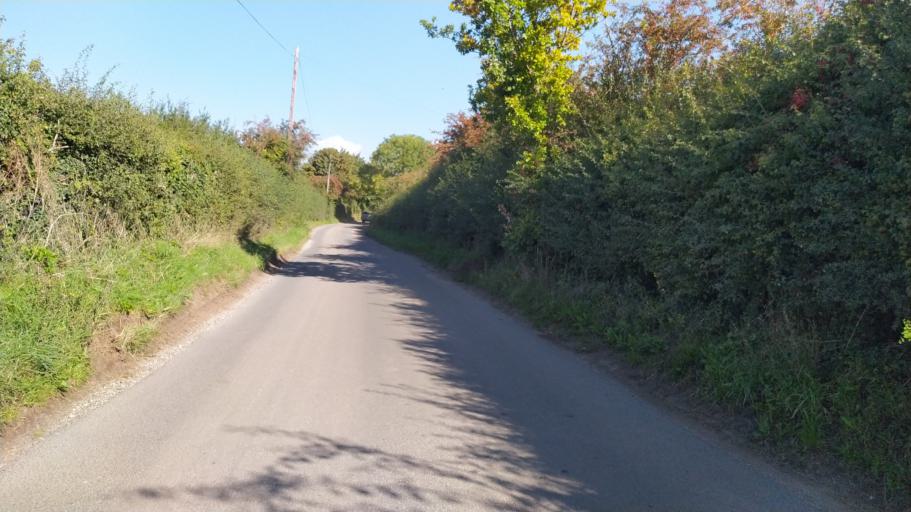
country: GB
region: England
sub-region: Hampshire
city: Abbotts Ann
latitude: 51.1685
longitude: -1.6041
